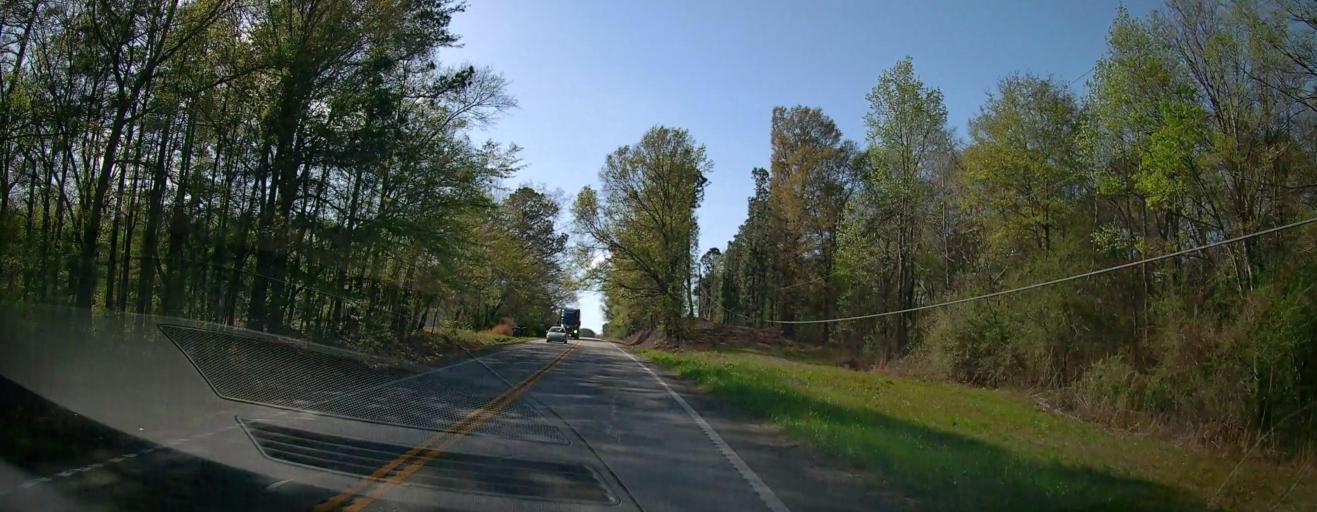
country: US
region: Georgia
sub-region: Baldwin County
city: Hardwick
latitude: 33.0907
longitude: -83.1779
